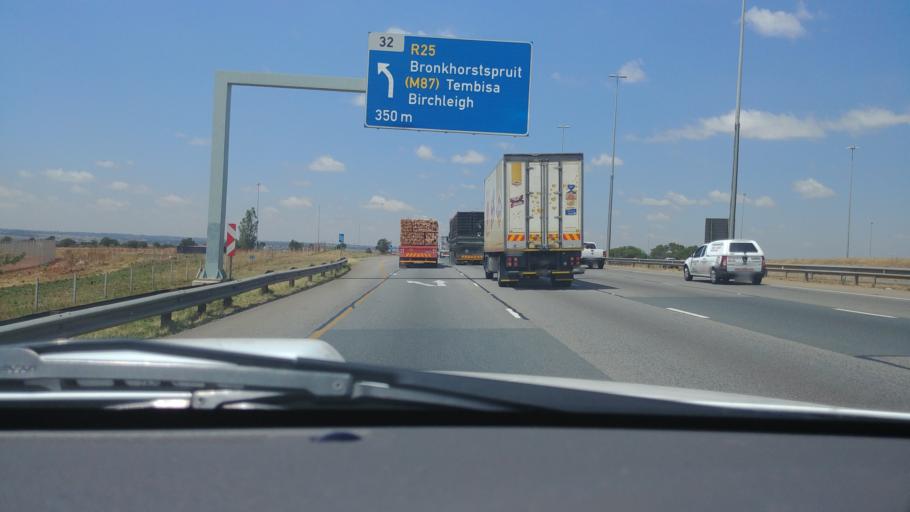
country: ZA
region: Gauteng
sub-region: Ekurhuleni Metropolitan Municipality
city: Tembisa
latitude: -26.0280
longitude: 28.2636
